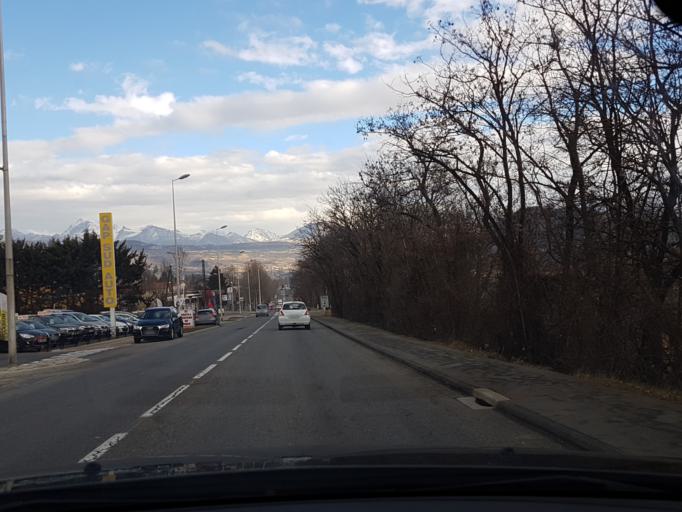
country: FR
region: Provence-Alpes-Cote d'Azur
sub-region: Departement des Hautes-Alpes
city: Gap
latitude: 44.5400
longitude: 6.0564
